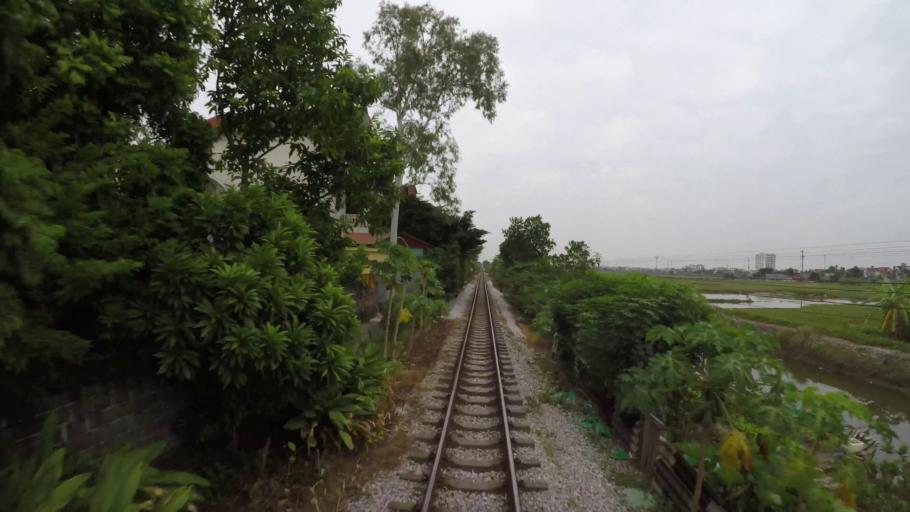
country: VN
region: Hai Phong
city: An Duong
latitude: 20.8964
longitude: 106.5846
